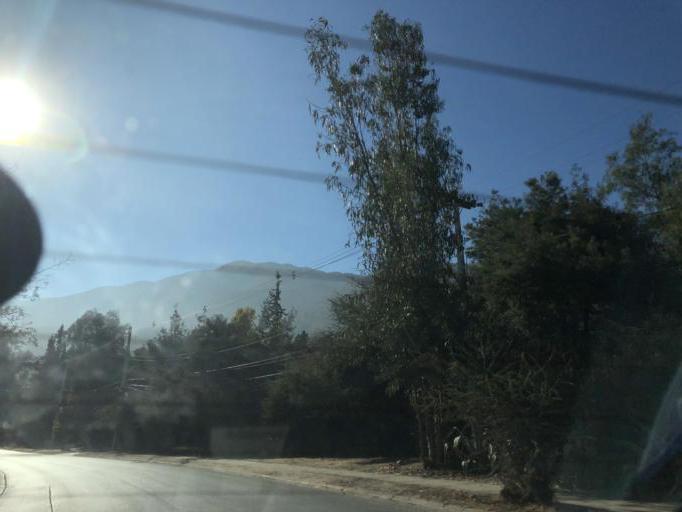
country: CL
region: Santiago Metropolitan
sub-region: Provincia de Cordillera
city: Puente Alto
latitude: -33.5604
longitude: -70.5360
